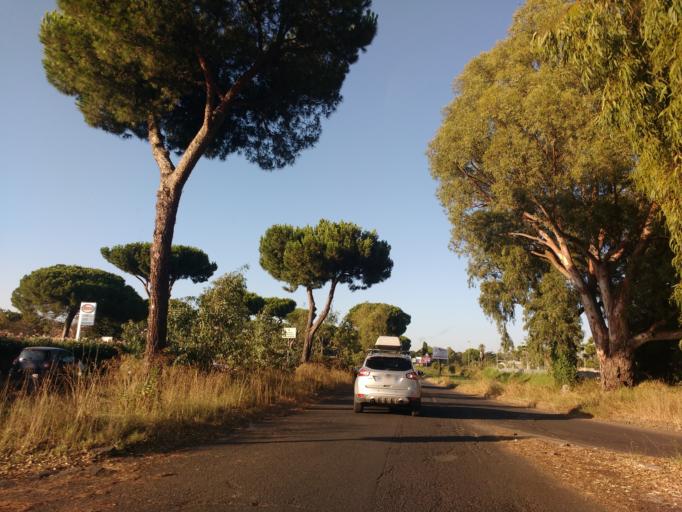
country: IT
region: Latium
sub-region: Citta metropolitana di Roma Capitale
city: Acilia-Castel Fusano-Ostia Antica
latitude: 41.7548
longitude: 12.3700
